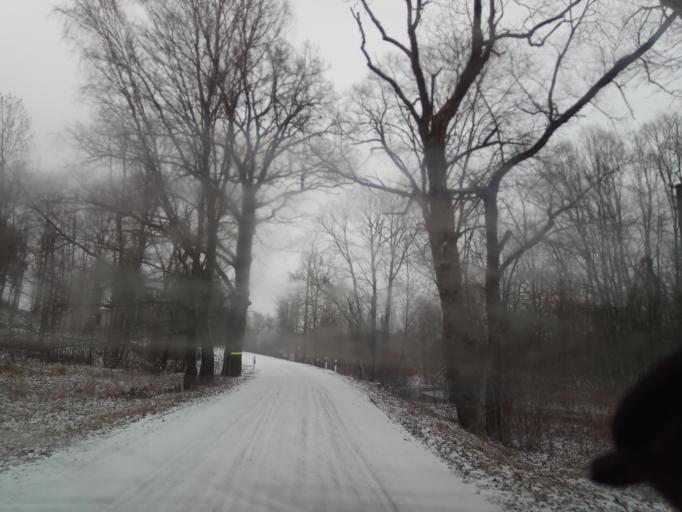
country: LT
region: Utenos apskritis
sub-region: Anyksciai
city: Anyksciai
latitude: 55.4229
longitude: 25.1113
